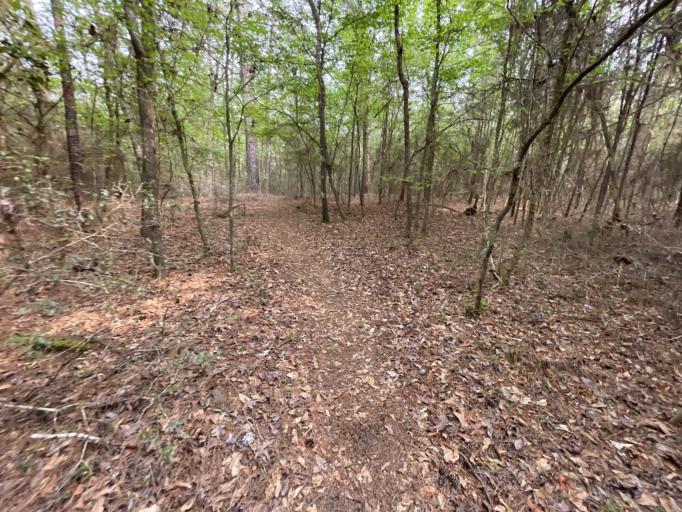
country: US
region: Texas
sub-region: Walker County
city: Huntsville
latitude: 30.6629
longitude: -95.4866
